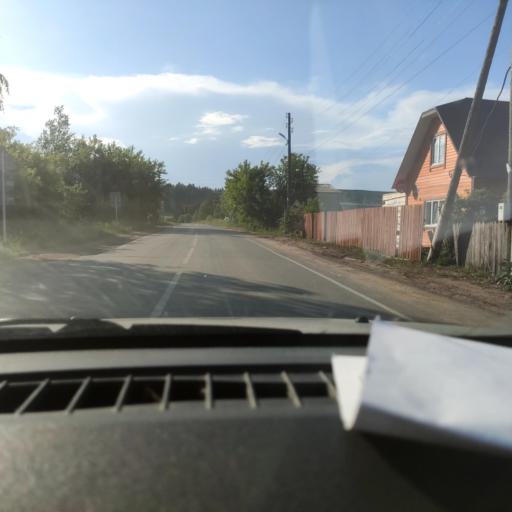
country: RU
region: Perm
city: Krasnokamsk
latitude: 58.1442
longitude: 55.7296
